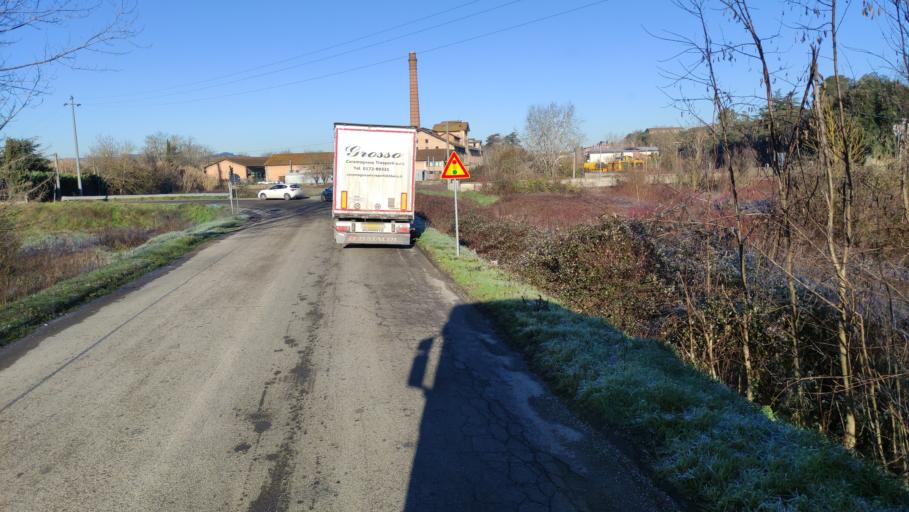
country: IT
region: Tuscany
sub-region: Province of Florence
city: Castelfiorentino
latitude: 43.6486
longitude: 10.9487
